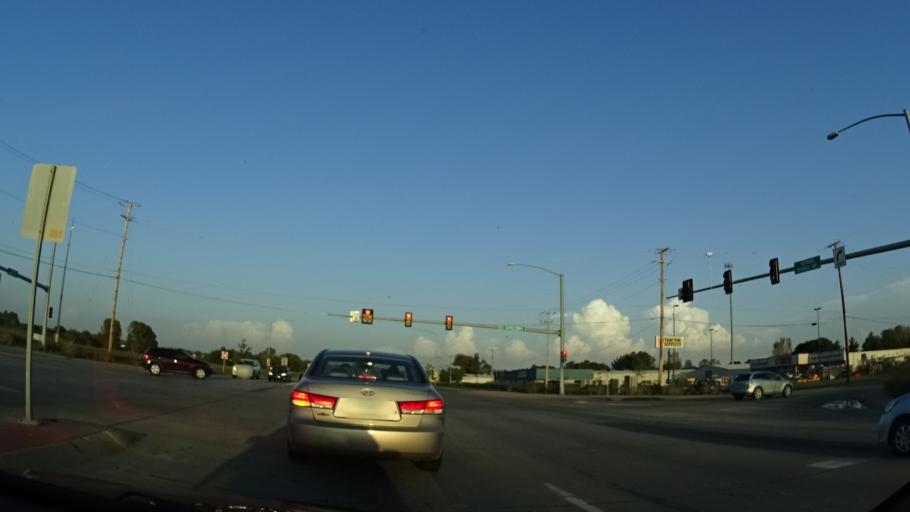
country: US
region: Iowa
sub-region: Pottawattamie County
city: Council Bluffs
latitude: 41.2197
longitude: -95.8511
